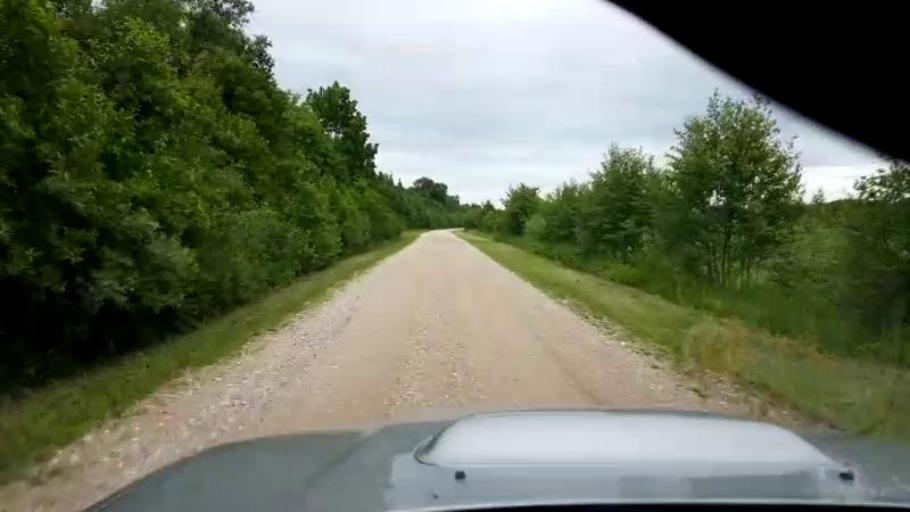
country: EE
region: Paernumaa
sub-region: Halinga vald
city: Parnu-Jaagupi
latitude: 58.5518
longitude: 24.5616
